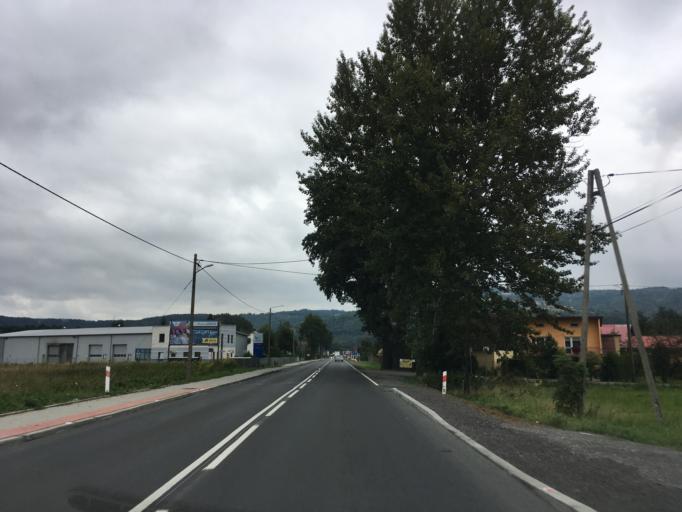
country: PL
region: Lesser Poland Voivodeship
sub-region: Powiat suski
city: Juszczyn
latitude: 49.7131
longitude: 19.6884
